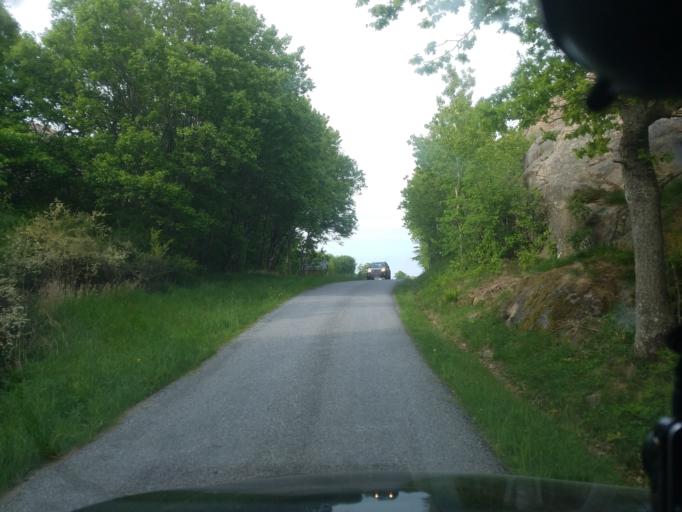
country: SE
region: Vaestra Goetaland
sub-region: Lysekils Kommun
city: Lysekil
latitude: 58.2993
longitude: 11.4491
